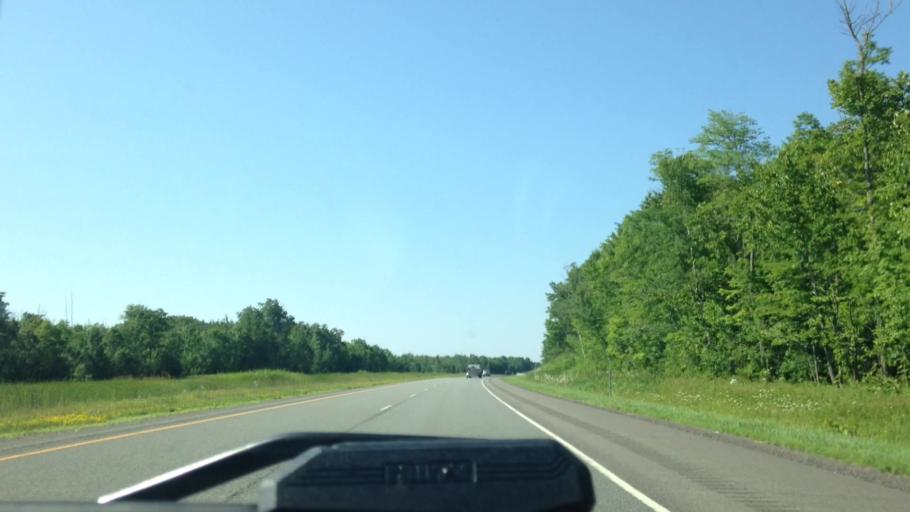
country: US
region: Wisconsin
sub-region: Douglas County
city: Lake Nebagamon
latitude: 46.4137
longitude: -91.8107
